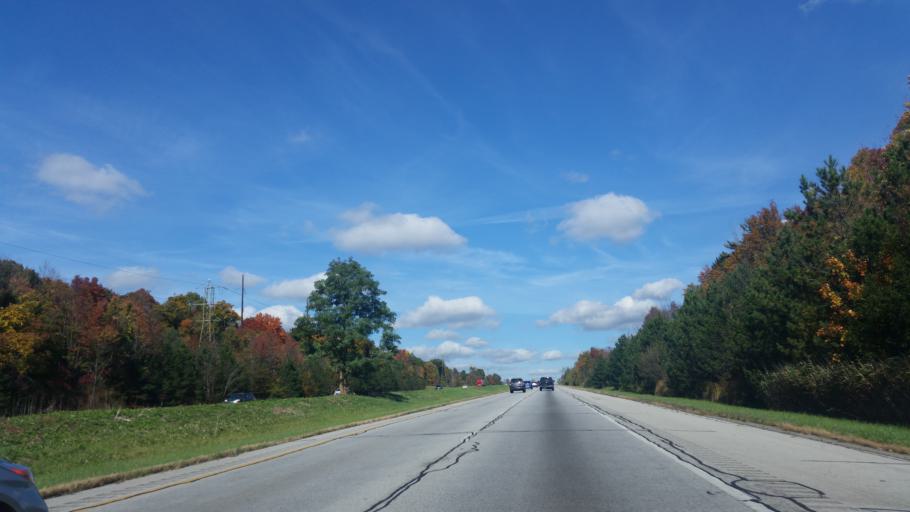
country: US
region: Ohio
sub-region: Summit County
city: Montrose-Ghent
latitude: 41.1758
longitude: -81.6257
